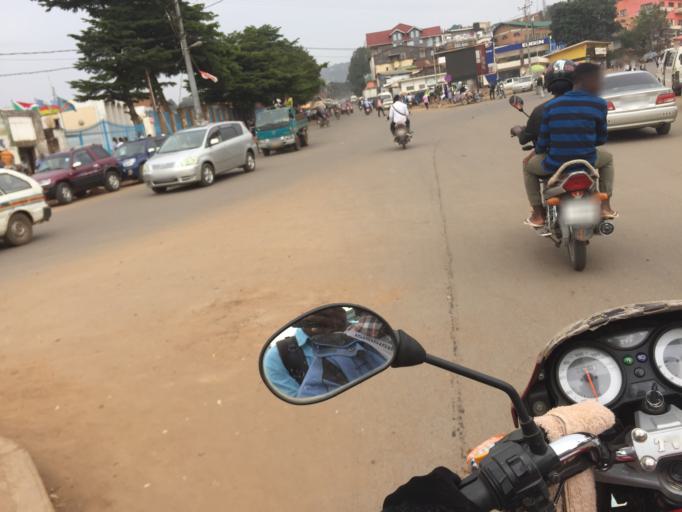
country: CD
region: South Kivu
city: Bukavu
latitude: -2.5060
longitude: 28.8622
